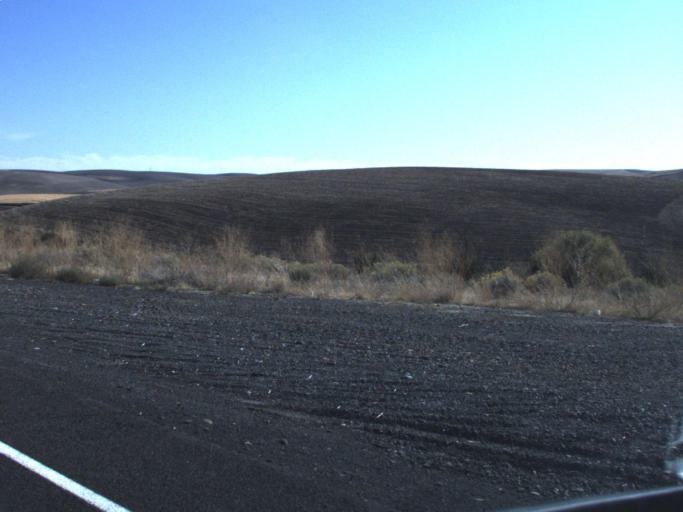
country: US
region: Washington
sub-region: Walla Walla County
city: Garrett
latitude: 46.2902
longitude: -118.5065
